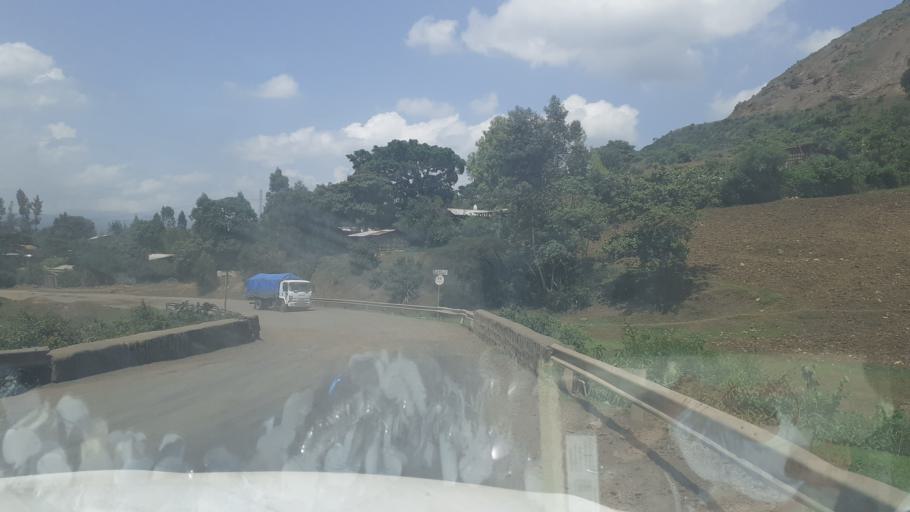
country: ET
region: Oromiya
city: Guder
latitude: 8.9748
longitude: 37.7532
